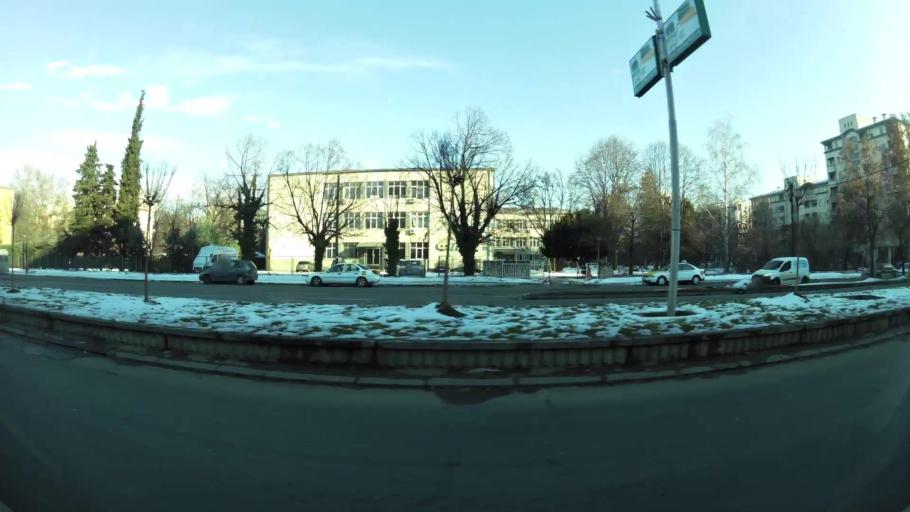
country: MK
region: Karpos
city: Skopje
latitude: 42.0004
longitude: 21.4045
